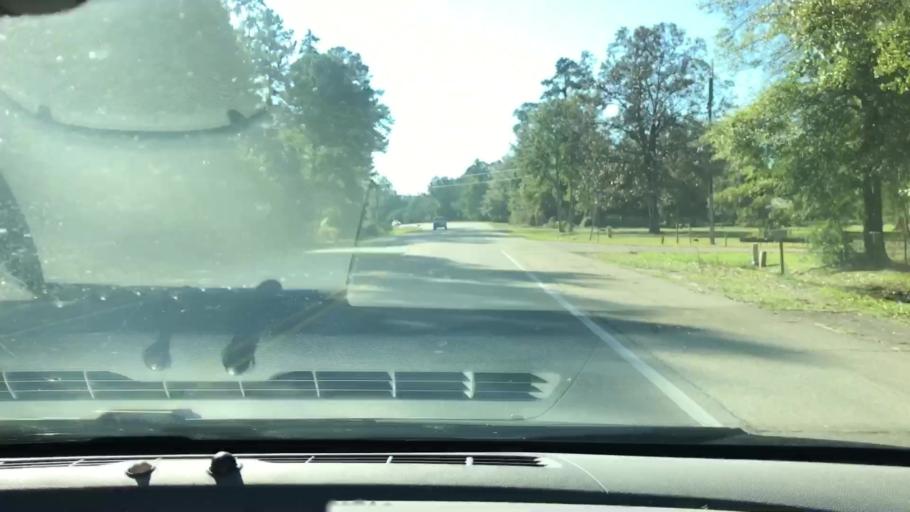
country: US
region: Louisiana
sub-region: Saint Tammany Parish
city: Pearl River
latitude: 30.4202
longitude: -89.7870
